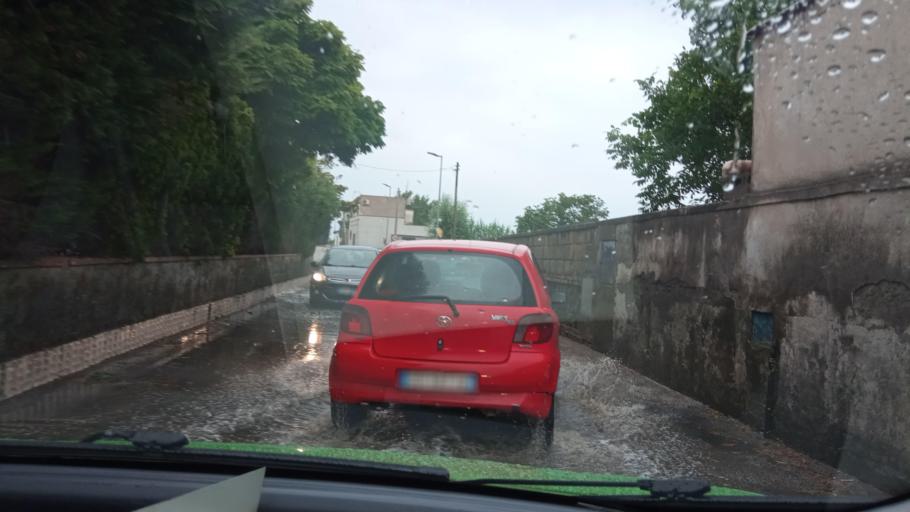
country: IT
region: Campania
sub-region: Provincia di Napoli
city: Pozzuoli
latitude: 40.8419
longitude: 14.1176
